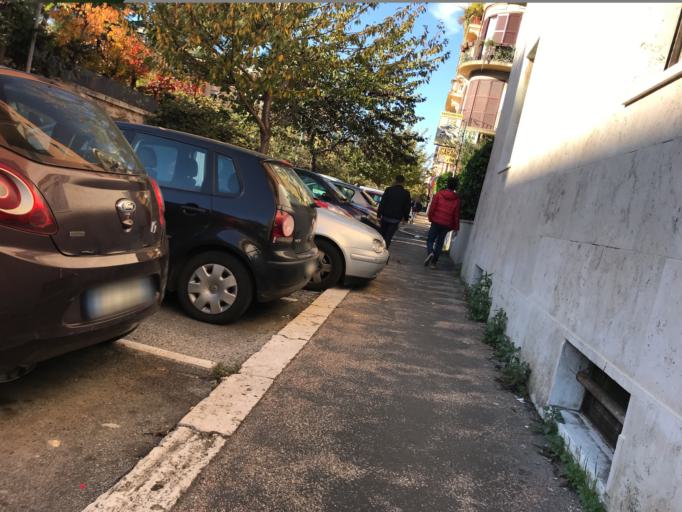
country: IT
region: Latium
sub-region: Citta metropolitana di Roma Capitale
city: Rome
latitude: 41.9078
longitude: 12.5150
